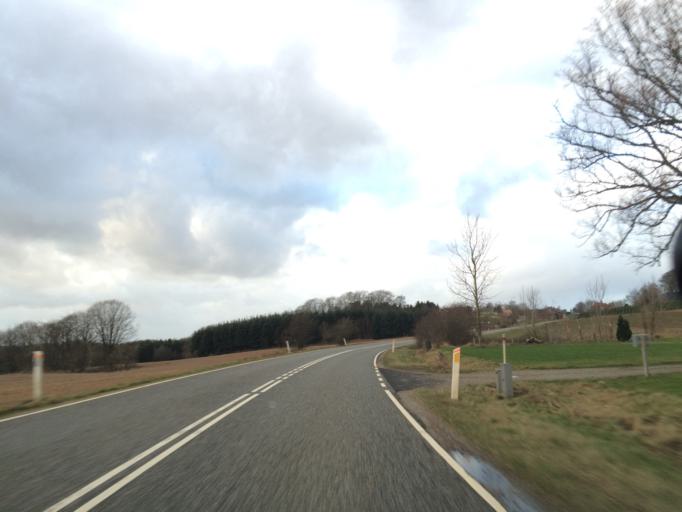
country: DK
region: Central Jutland
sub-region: Silkeborg Kommune
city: Svejbaek
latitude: 56.0969
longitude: 9.6122
